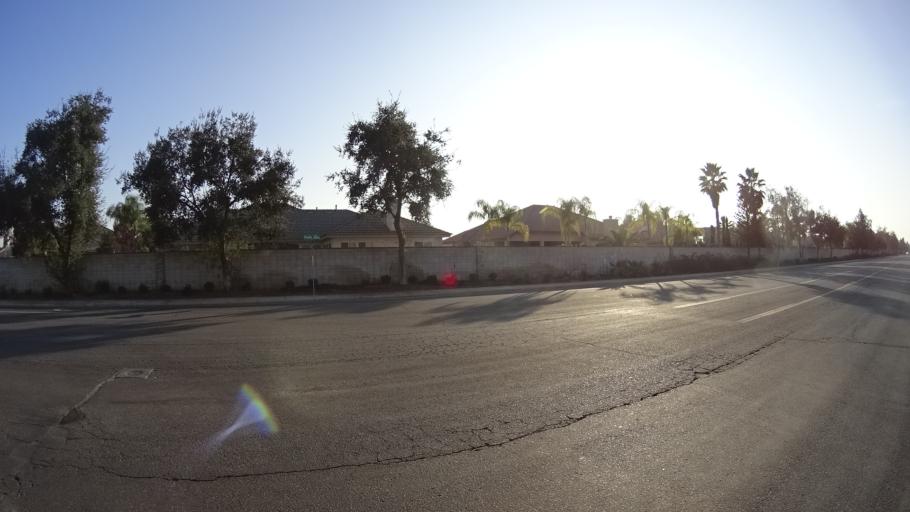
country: US
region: California
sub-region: Kern County
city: Rosedale
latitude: 35.3763
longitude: -119.1464
